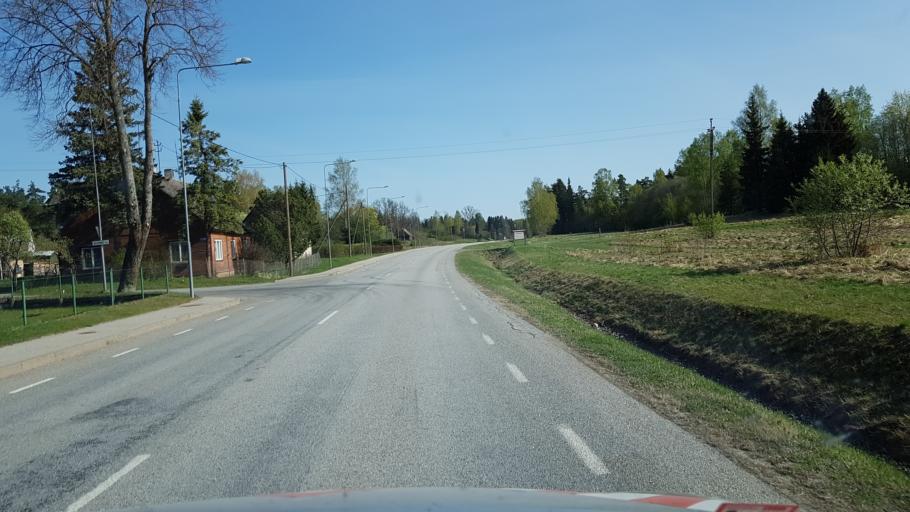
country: EE
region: Viljandimaa
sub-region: Abja vald
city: Abja-Paluoja
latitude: 58.1306
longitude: 25.3637
